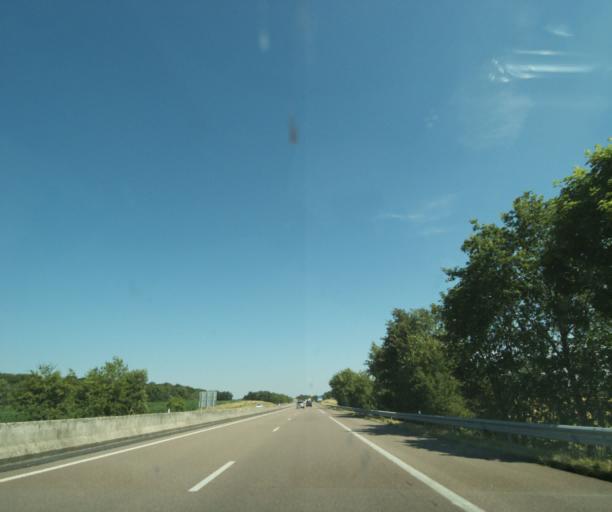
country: FR
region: Lorraine
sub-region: Departement de Meurthe-et-Moselle
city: Colombey-les-Belles
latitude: 48.4156
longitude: 5.8643
